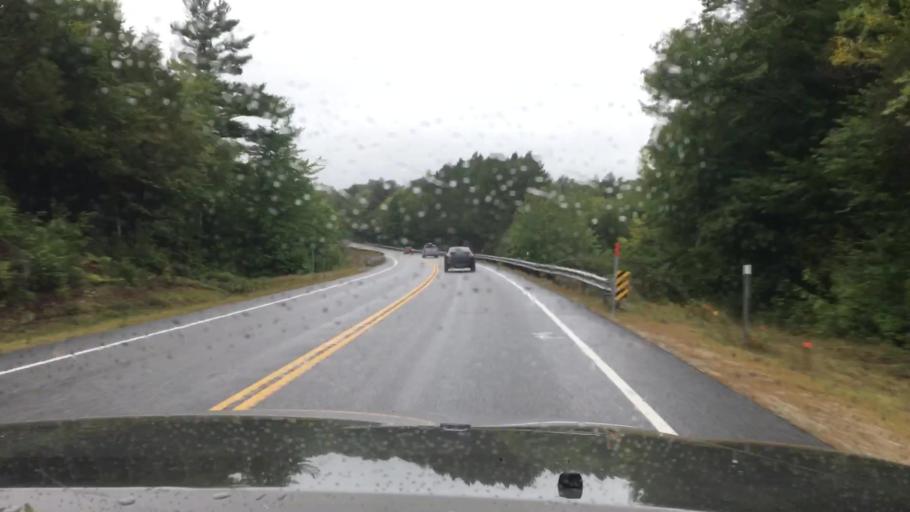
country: US
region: New Hampshire
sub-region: Cheshire County
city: Harrisville
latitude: 43.0602
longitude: -72.0748
